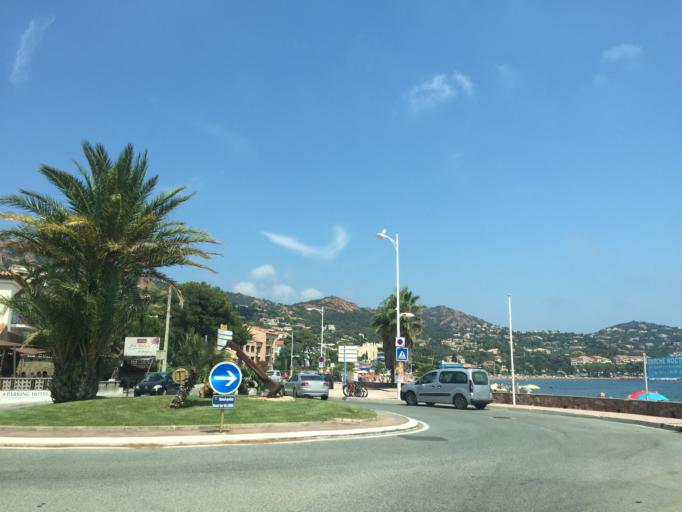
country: FR
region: Provence-Alpes-Cote d'Azur
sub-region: Departement du Var
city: Saint-Raphael
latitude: 43.4334
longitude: 6.8590
